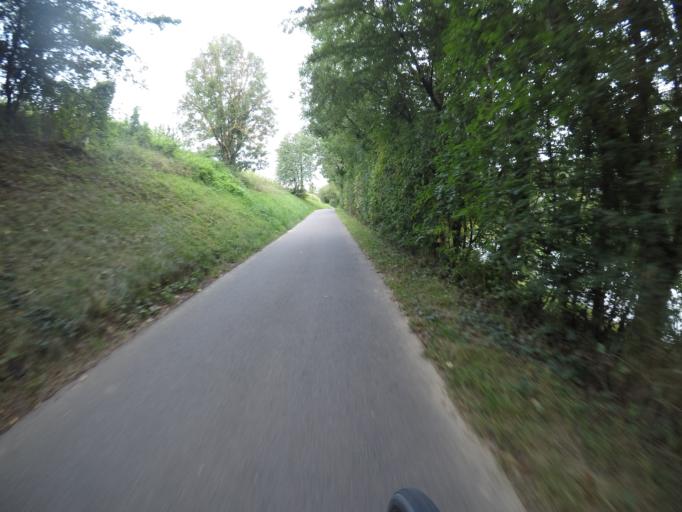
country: DE
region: Baden-Wuerttemberg
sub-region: Regierungsbezirk Stuttgart
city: Marbach am Neckar
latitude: 48.8871
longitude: 9.2705
